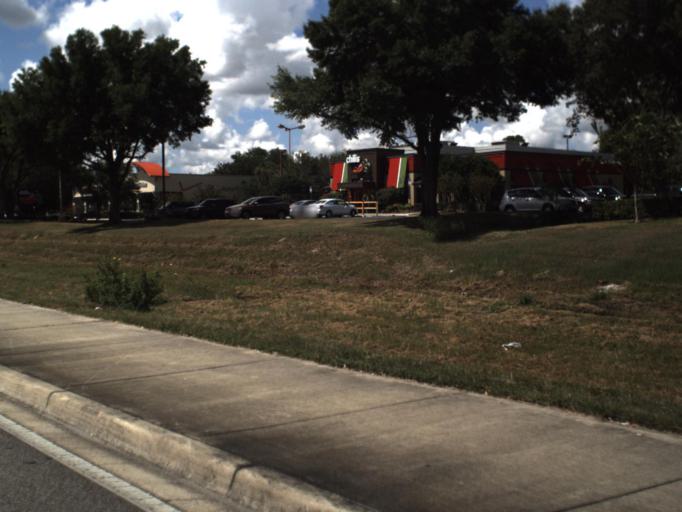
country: US
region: Florida
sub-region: Polk County
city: Gibsonia
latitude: 28.0946
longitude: -81.9740
